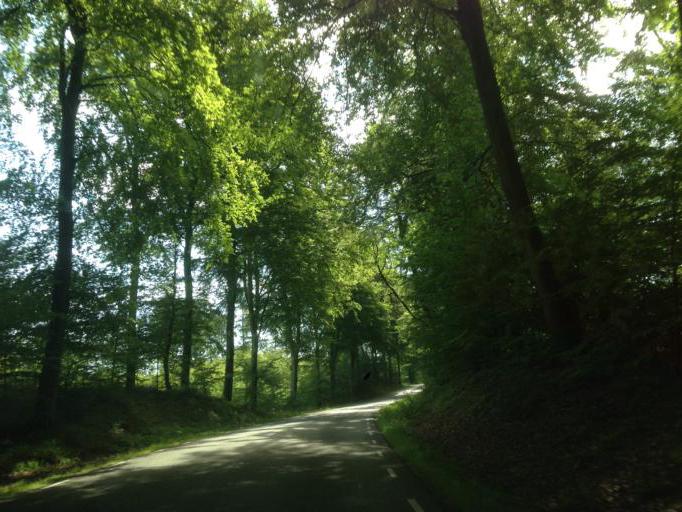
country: SE
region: Skane
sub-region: Tomelilla Kommun
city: Tomelilla
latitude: 55.6438
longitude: 14.0490
